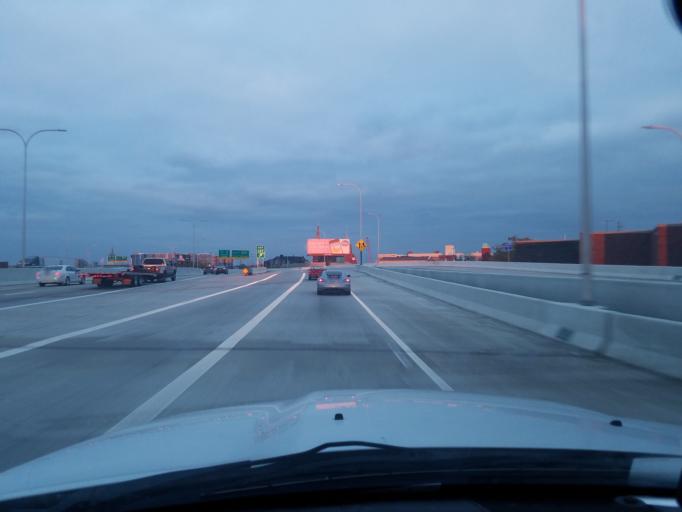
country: US
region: Kentucky
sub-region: Jefferson County
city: Louisville
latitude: 38.2523
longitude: -85.7460
